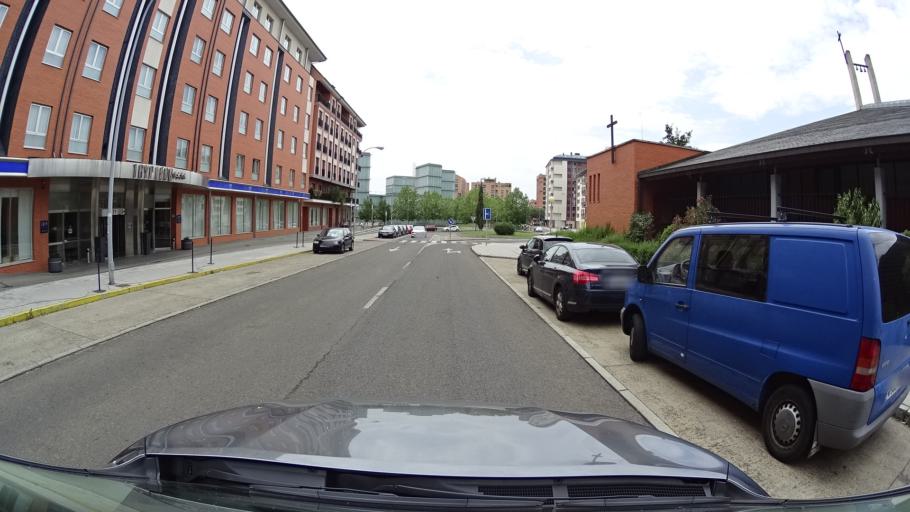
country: ES
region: Castille and Leon
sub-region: Provincia de Leon
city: Leon
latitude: 42.6079
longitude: -5.5814
